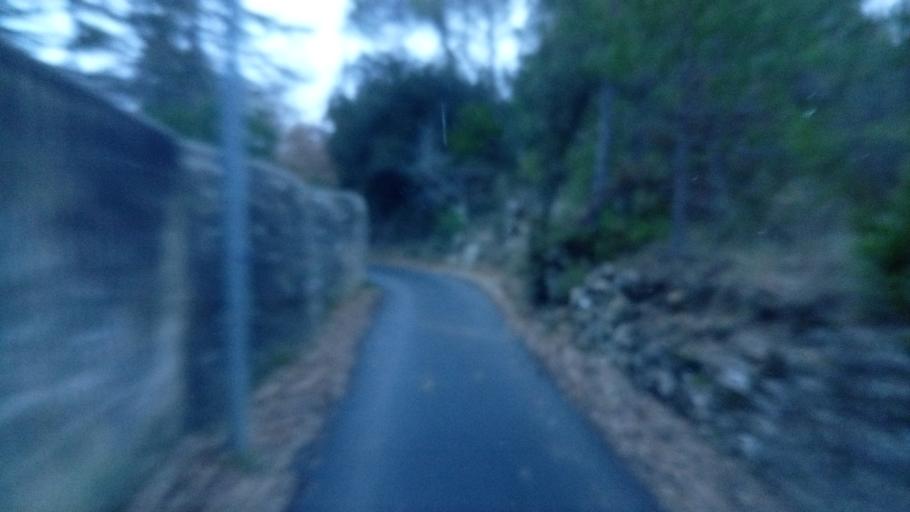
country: FR
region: Provence-Alpes-Cote d'Azur
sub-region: Departement du Var
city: Saint-Julien
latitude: 43.6368
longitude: 5.9436
